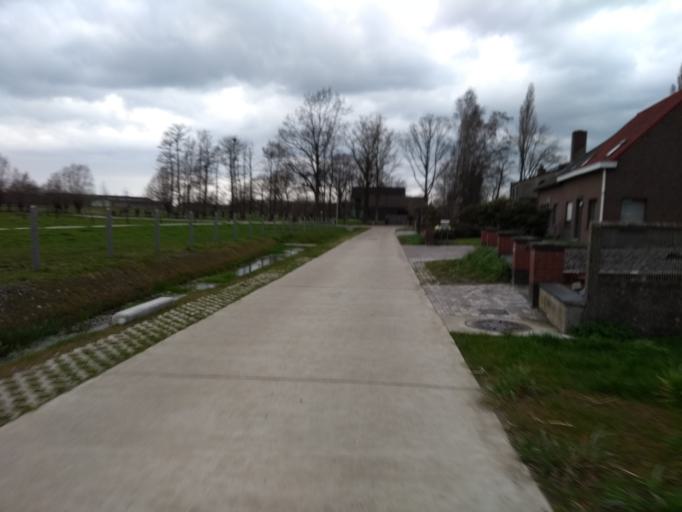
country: BE
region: Flanders
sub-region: Provincie Oost-Vlaanderen
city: Aalter
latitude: 51.0919
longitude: 3.4368
